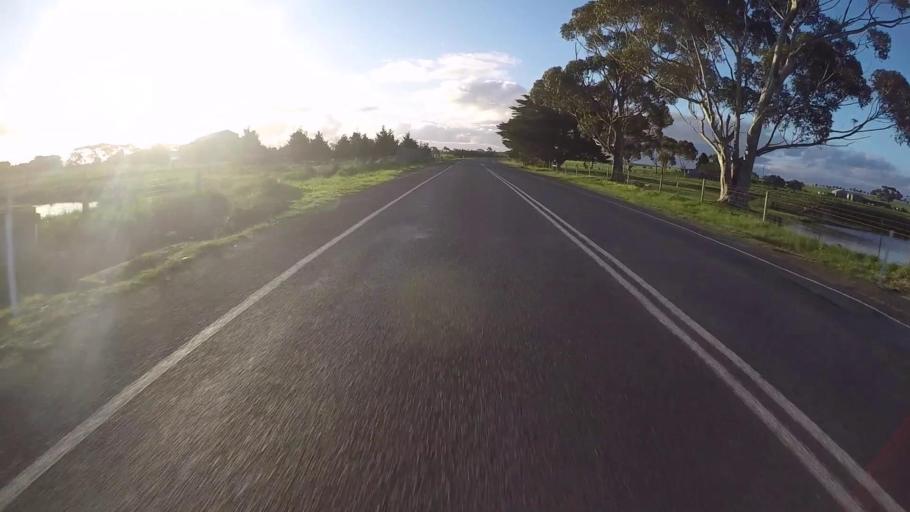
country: AU
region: Victoria
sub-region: Greater Geelong
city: Wandana Heights
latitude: -38.1364
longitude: 144.2867
